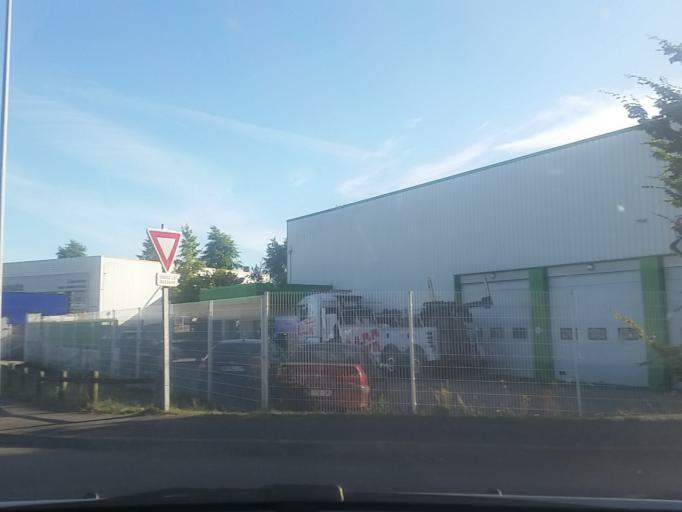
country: FR
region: Pays de la Loire
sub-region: Departement de la Loire-Atlantique
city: Bouguenais
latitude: 47.1770
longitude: -1.6134
